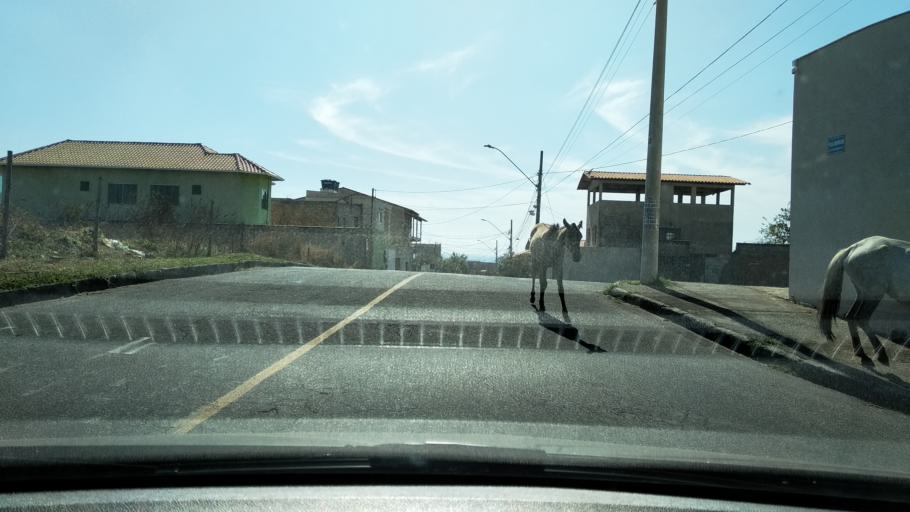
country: BR
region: Minas Gerais
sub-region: Belo Horizonte
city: Belo Horizonte
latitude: -19.8620
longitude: -43.8819
